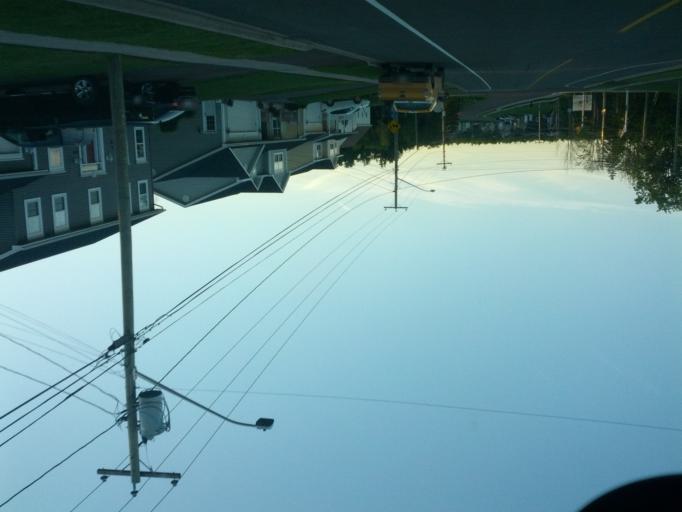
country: CA
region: New Brunswick
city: Moncton
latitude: 46.1082
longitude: -64.8709
